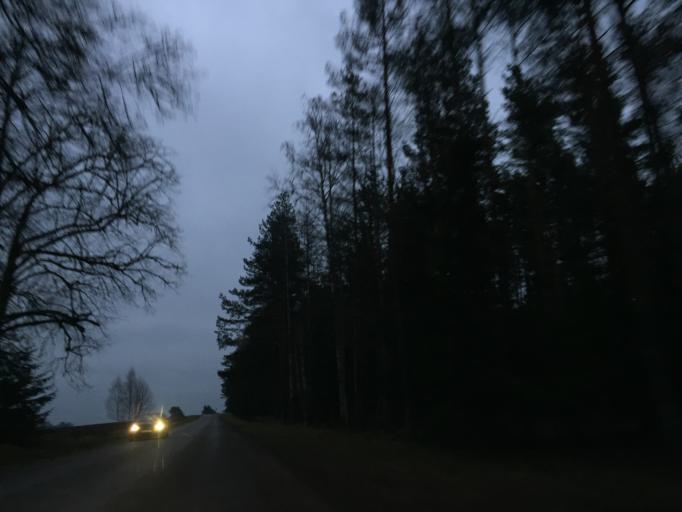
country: LV
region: Koceni
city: Koceni
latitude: 57.5515
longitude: 25.2379
